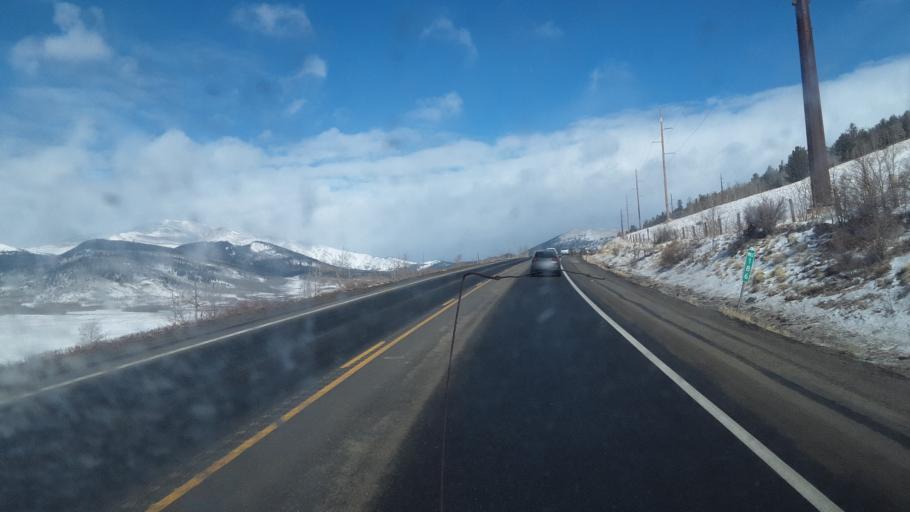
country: US
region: Colorado
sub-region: Park County
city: Fairplay
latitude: 39.2554
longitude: -105.9632
